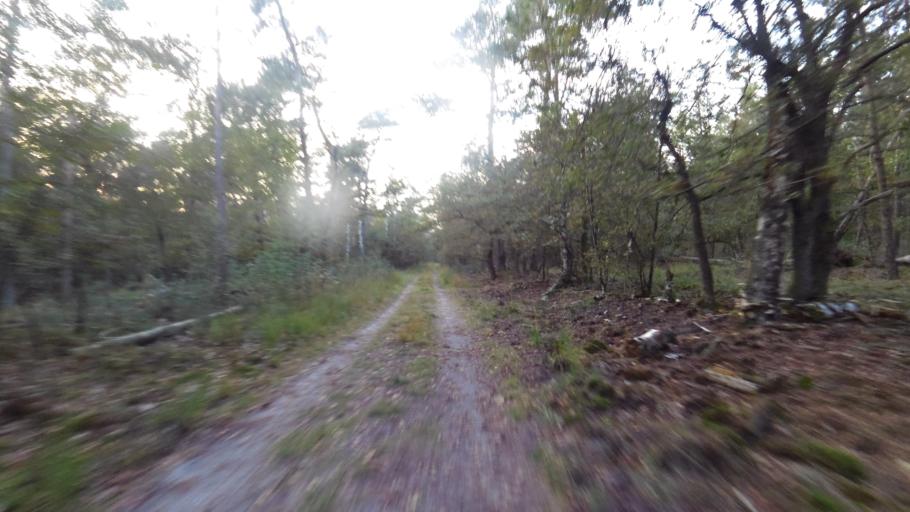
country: NL
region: Gelderland
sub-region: Gemeente Nunspeet
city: Nunspeet
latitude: 52.3279
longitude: 5.7965
